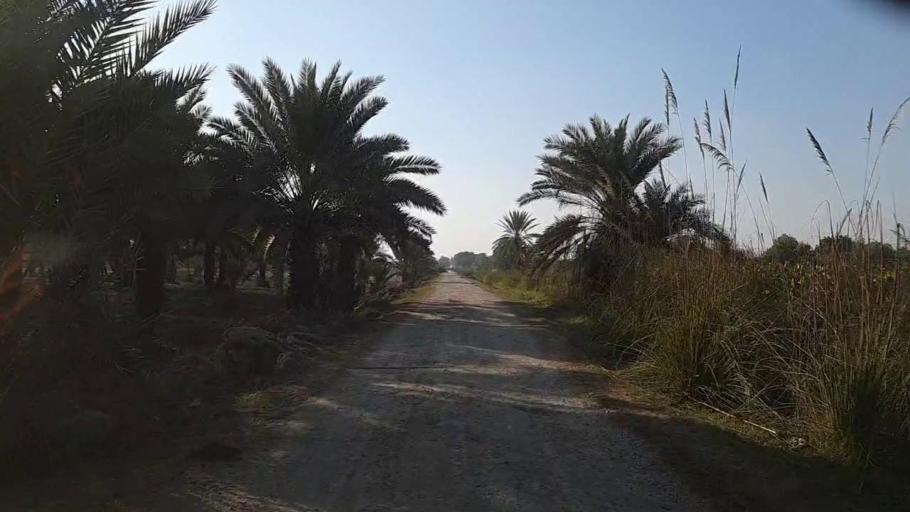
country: PK
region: Sindh
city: Ranipur
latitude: 27.2537
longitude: 68.5344
